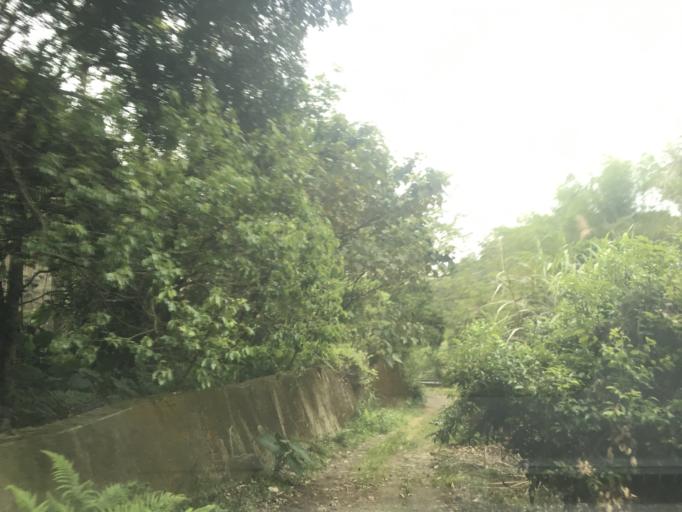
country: TW
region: Taiwan
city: Zhongxing New Village
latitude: 24.0344
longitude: 120.7839
